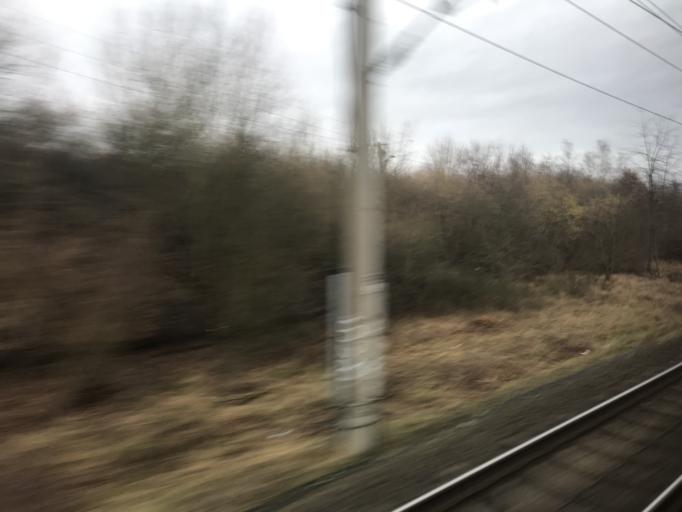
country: DE
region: Lower Saxony
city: Weyhausen
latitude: 52.4221
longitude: 10.6908
